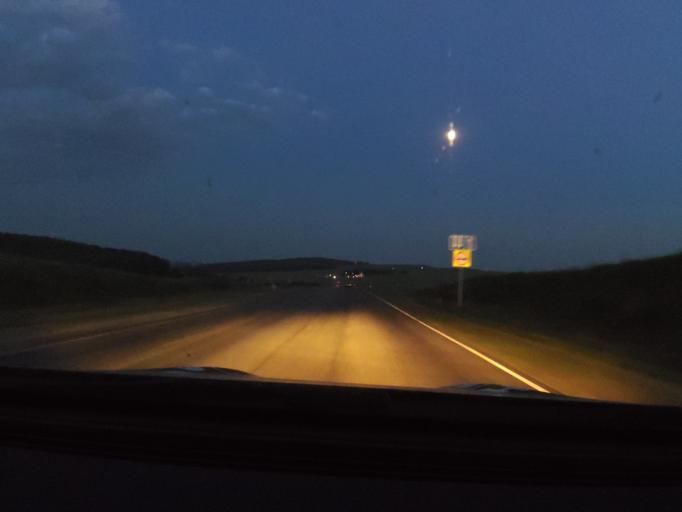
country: RU
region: Bashkortostan
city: Duvan
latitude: 55.9280
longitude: 58.2034
